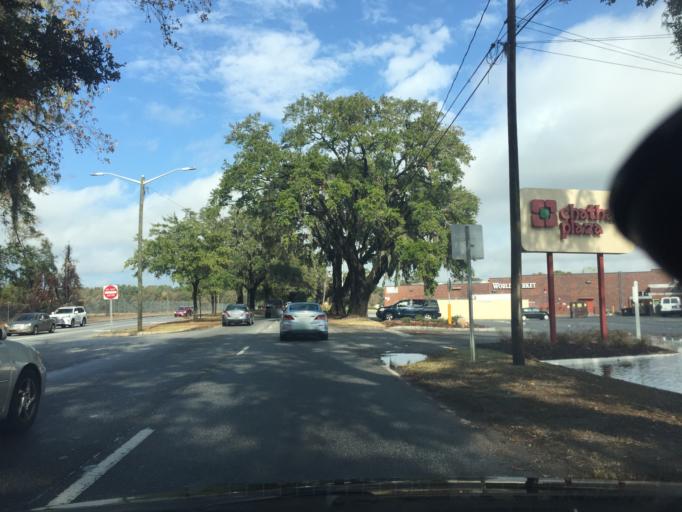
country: US
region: Georgia
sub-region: Chatham County
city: Isle of Hope
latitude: 32.0057
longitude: -81.1196
